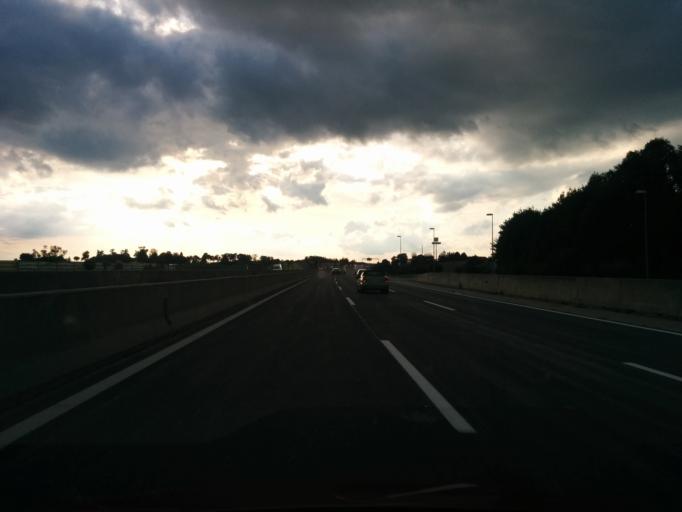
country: AT
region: Lower Austria
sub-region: Politischer Bezirk Amstetten
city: Wolfsbach
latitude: 48.1125
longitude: 14.6767
